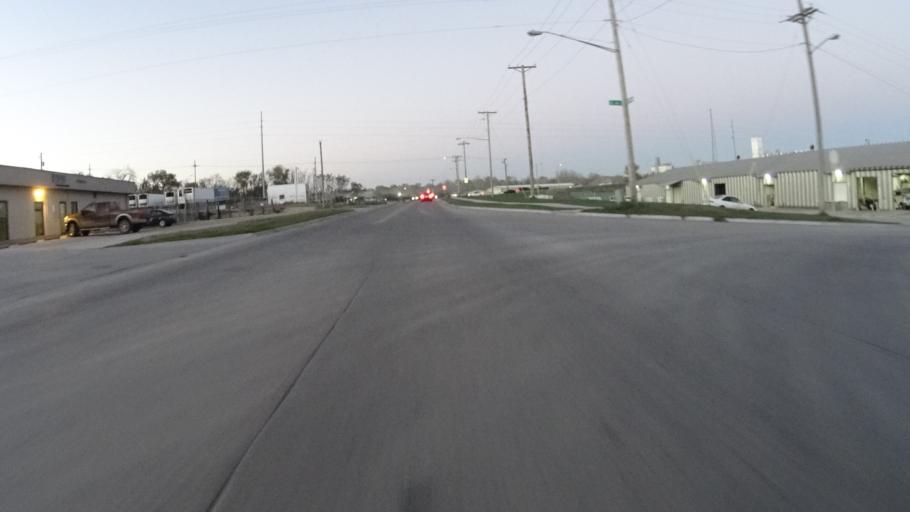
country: US
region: Nebraska
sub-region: Douglas County
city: Omaha
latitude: 41.2183
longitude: -95.9604
